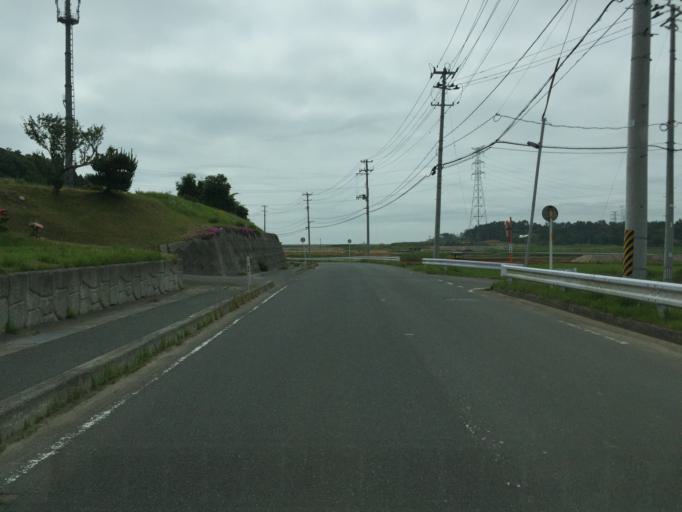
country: JP
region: Fukushima
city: Namie
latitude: 37.6638
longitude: 141.0108
